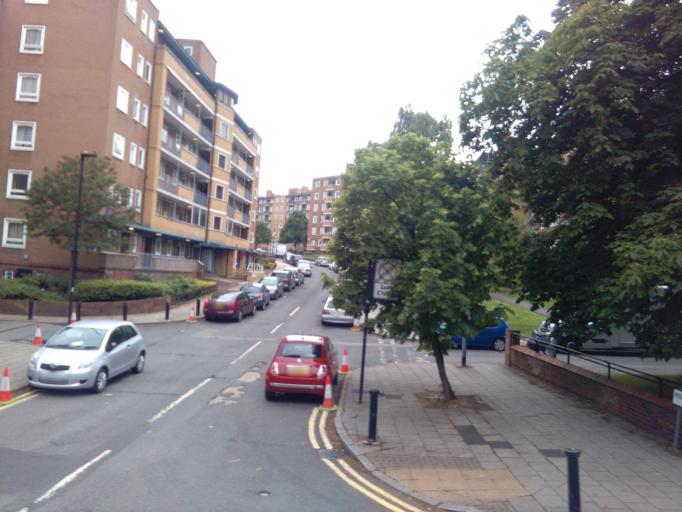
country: GB
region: England
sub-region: Greater London
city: Brixton Hill
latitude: 51.4428
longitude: -0.1098
